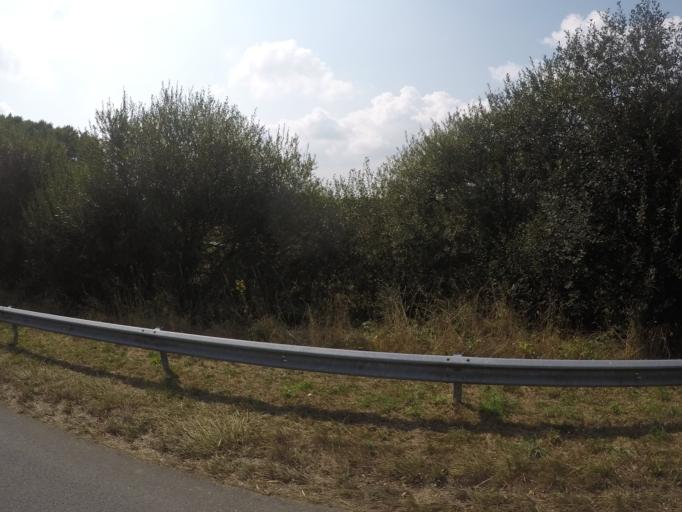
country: FR
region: Brittany
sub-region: Departement des Cotes-d'Armor
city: Tremuson
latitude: 48.5259
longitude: -2.8979
